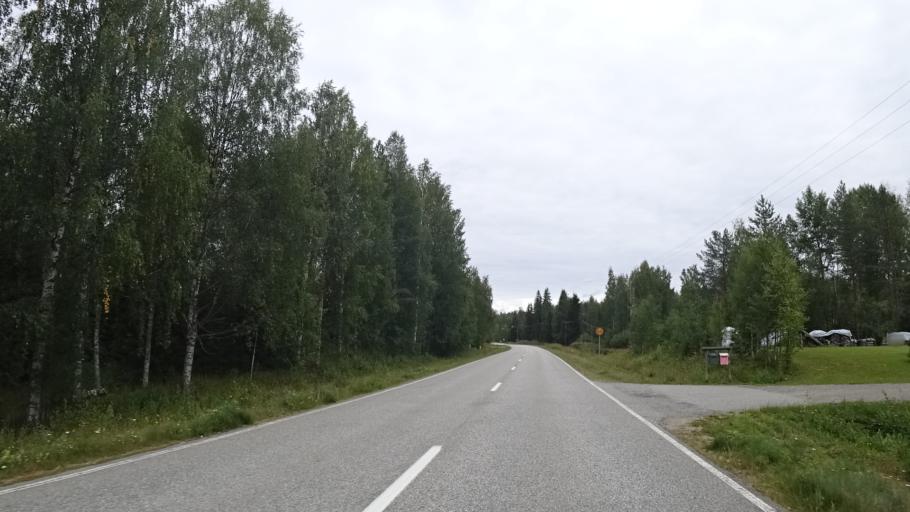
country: FI
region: North Karelia
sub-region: Joensuu
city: Ilomantsi
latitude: 62.6367
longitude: 31.2834
